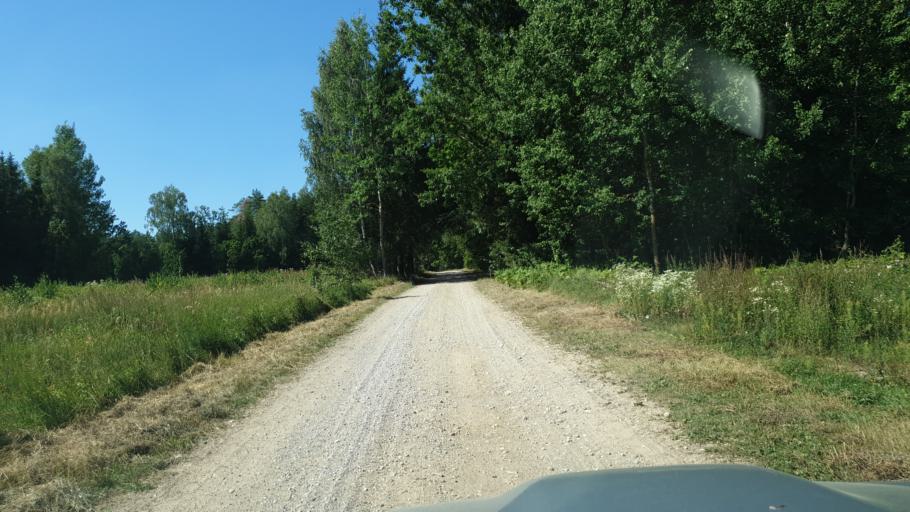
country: LT
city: Sirvintos
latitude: 54.9003
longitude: 24.8943
